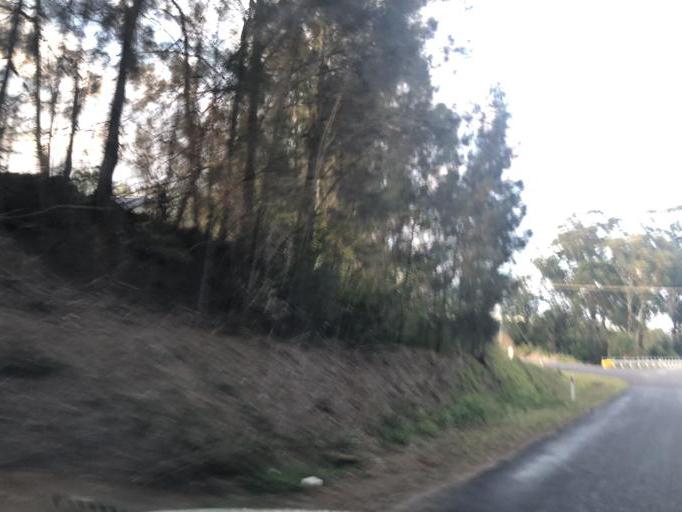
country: AU
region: New South Wales
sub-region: Nambucca Shire
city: Macksville
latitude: -30.7289
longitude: 152.9157
